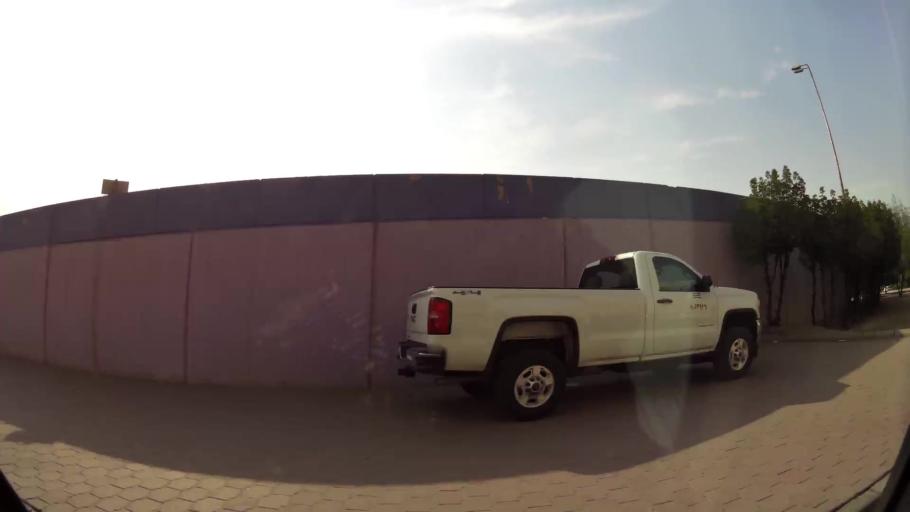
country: KW
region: Al Farwaniyah
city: Al Farwaniyah
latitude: 29.2860
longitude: 47.9676
